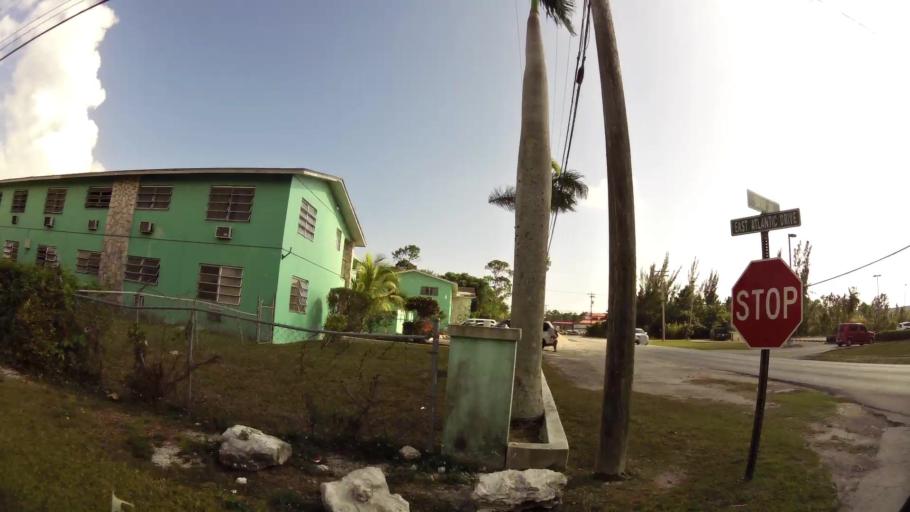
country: BS
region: Freeport
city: Freeport
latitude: 26.5192
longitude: -78.6925
